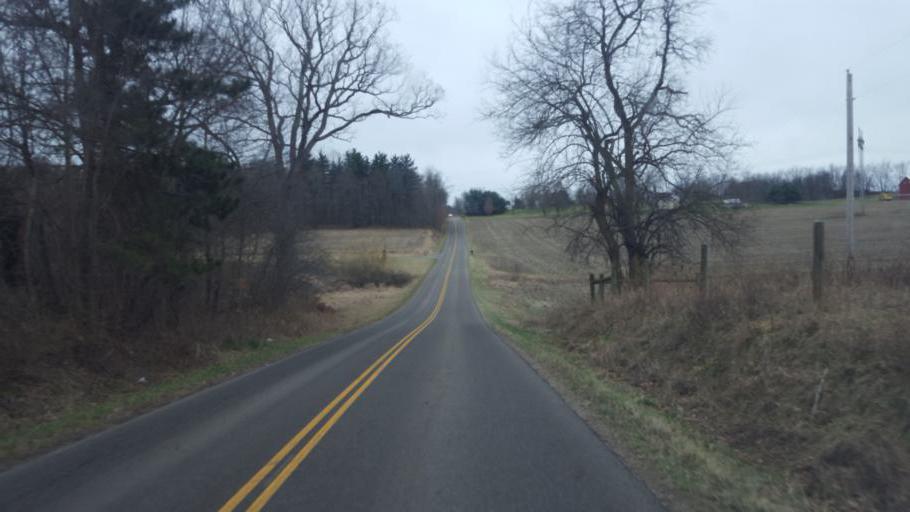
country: US
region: Ohio
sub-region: Knox County
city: Fredericktown
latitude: 40.4653
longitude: -82.4845
